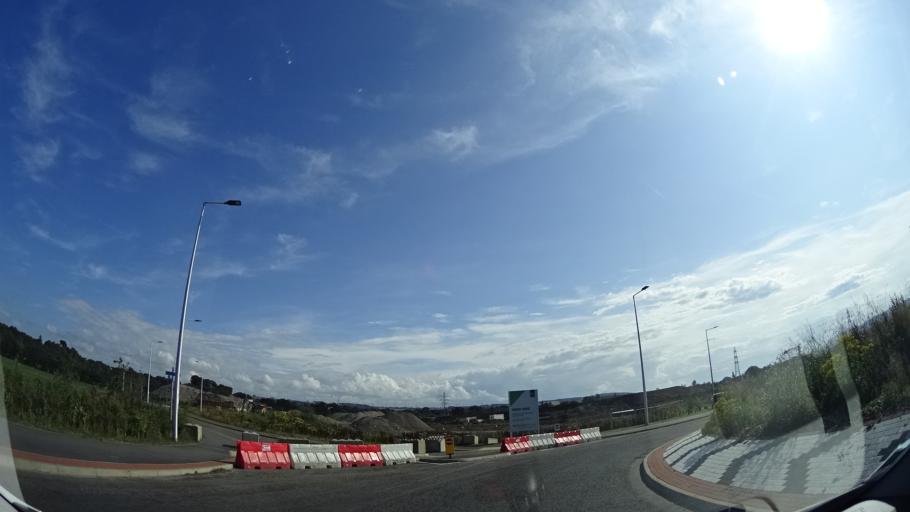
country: GB
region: Scotland
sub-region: Highland
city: Inverness
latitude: 57.4580
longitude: -4.2478
